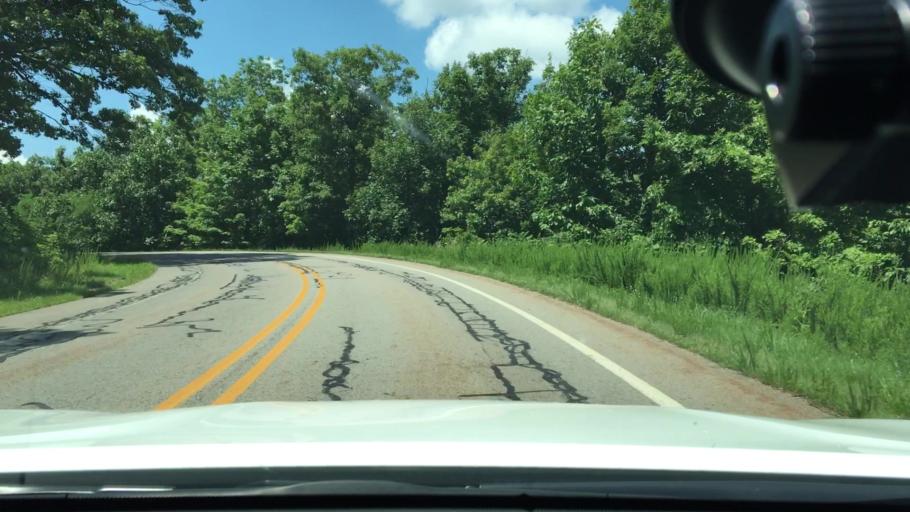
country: US
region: Arkansas
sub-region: Logan County
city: Paris
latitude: 35.1697
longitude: -93.6343
